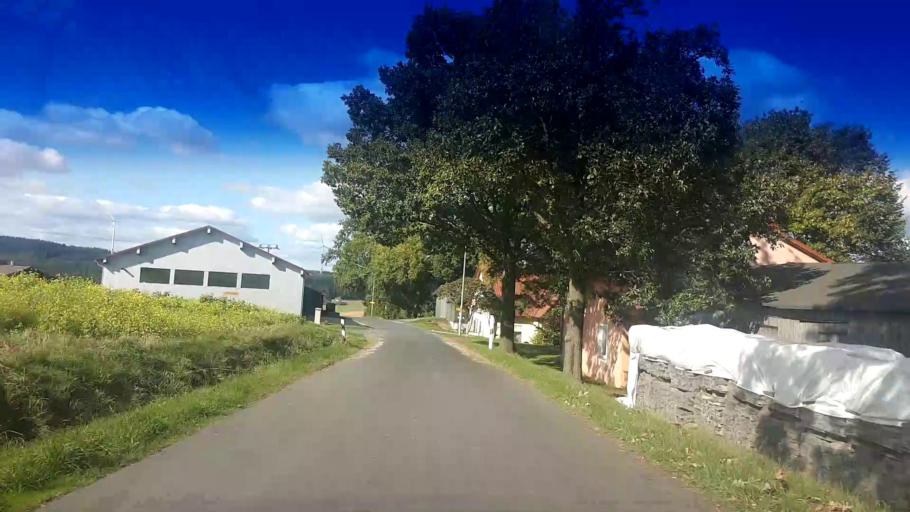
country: DE
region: Bavaria
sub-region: Upper Franconia
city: Schirnding
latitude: 50.0258
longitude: 12.2350
